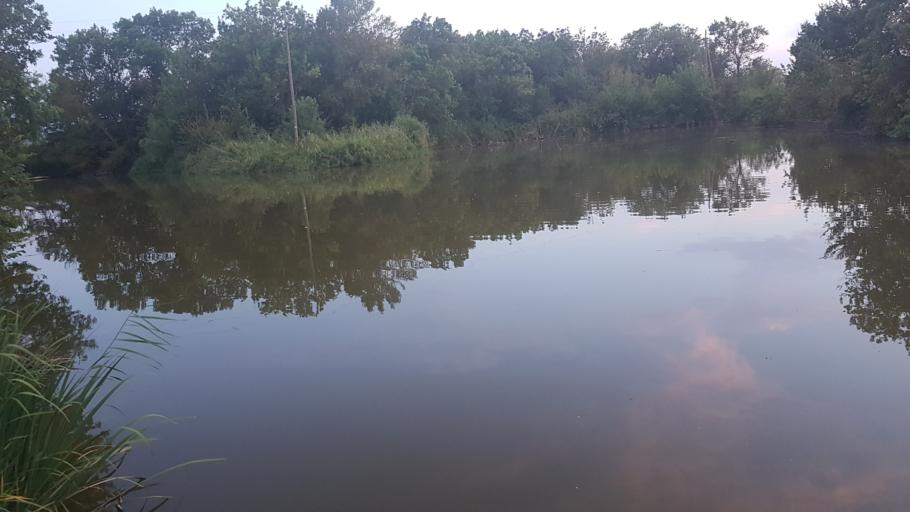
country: ES
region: Catalonia
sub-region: Provincia de Girona
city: Pals
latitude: 42.0082
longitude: 3.1884
